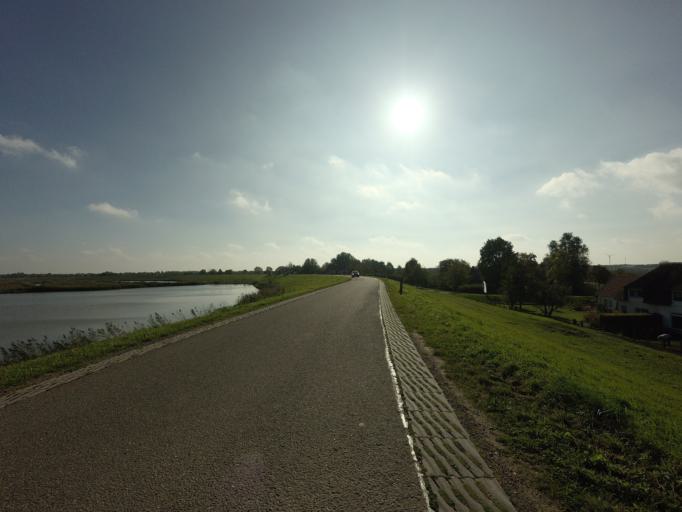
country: NL
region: Gelderland
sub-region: Gemeente Culemborg
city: Culemborg
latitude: 51.9578
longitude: 5.1998
